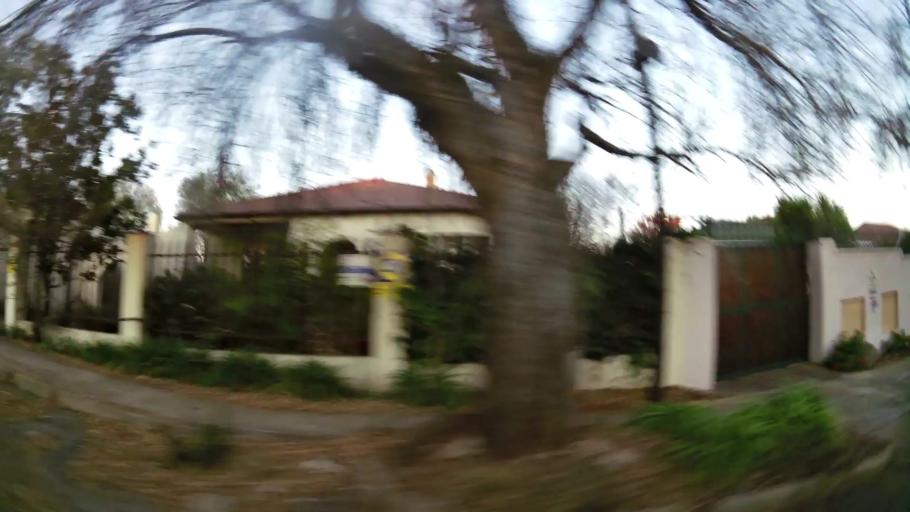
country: ZA
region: Gauteng
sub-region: City of Johannesburg Metropolitan Municipality
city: Roodepoort
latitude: -26.1723
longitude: 27.9153
